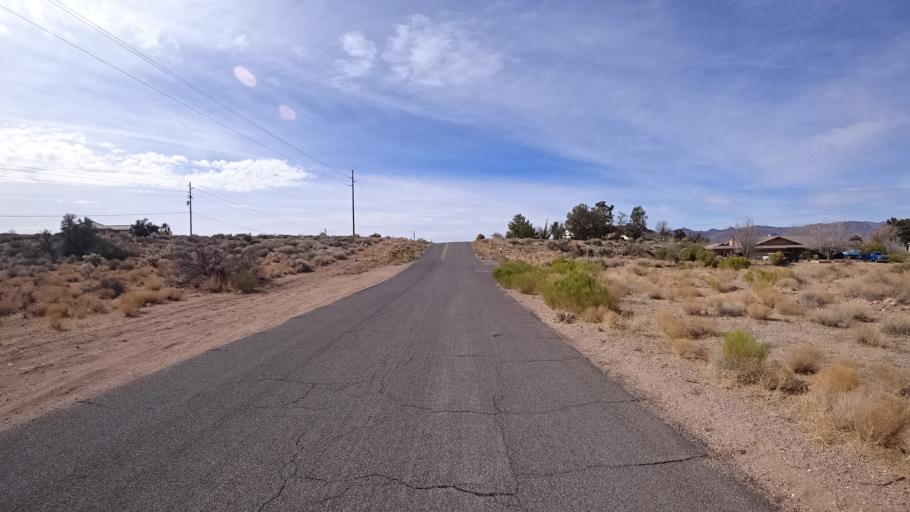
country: US
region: Arizona
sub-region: Mohave County
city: Kingman
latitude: 35.1814
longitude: -113.9882
